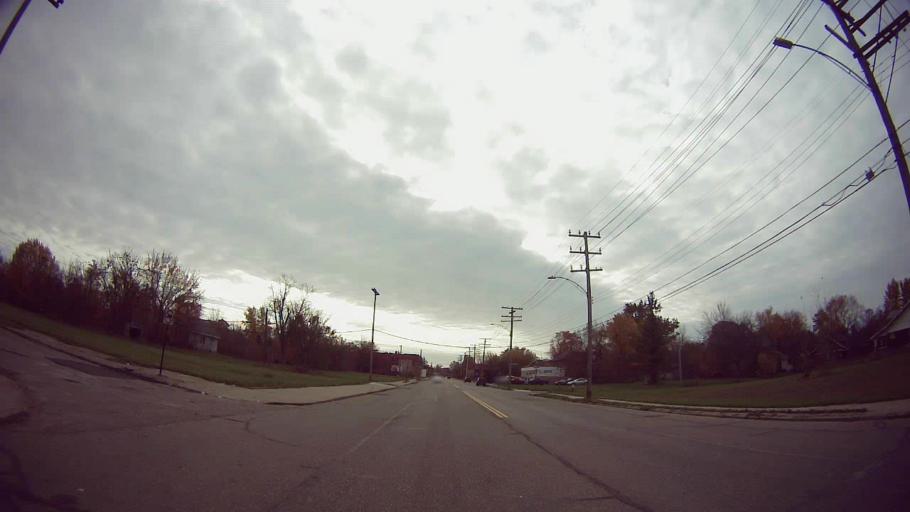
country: US
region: Michigan
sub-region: Wayne County
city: Highland Park
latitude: 42.4232
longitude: -83.1020
